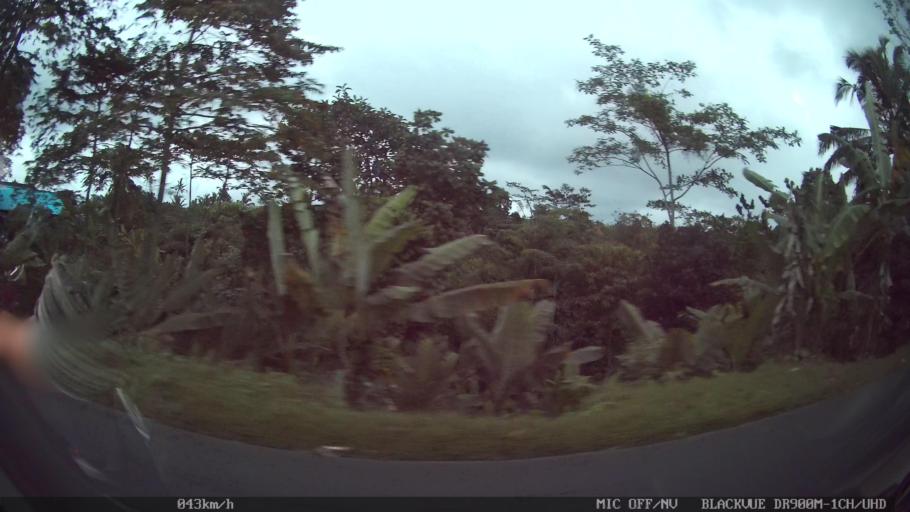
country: ID
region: Bali
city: Empalan
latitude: -8.3878
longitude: 115.1511
